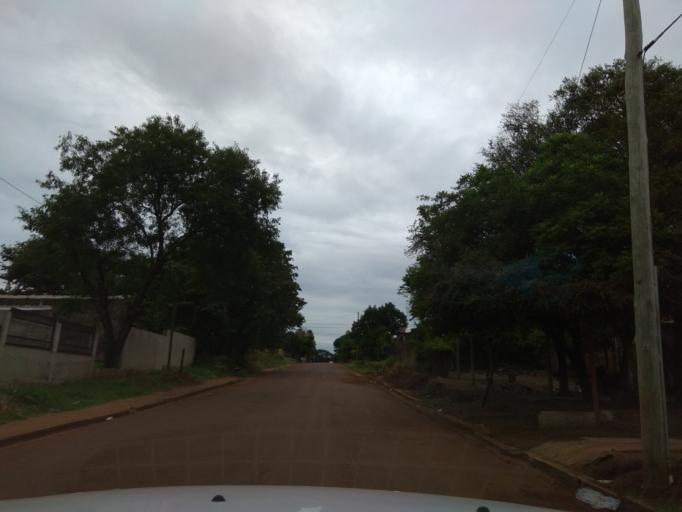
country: AR
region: Misiones
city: Garupa
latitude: -27.4436
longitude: -55.8675
